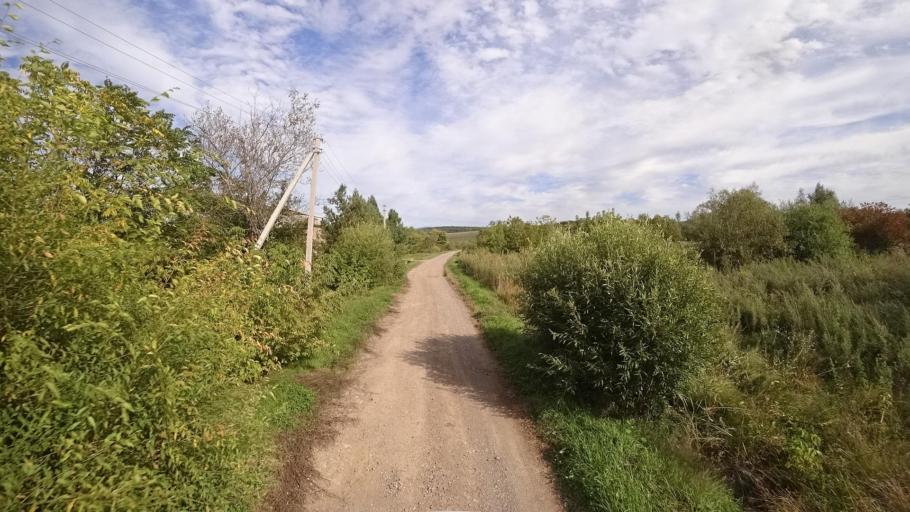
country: RU
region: Primorskiy
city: Dostoyevka
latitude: 44.3270
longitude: 133.4969
